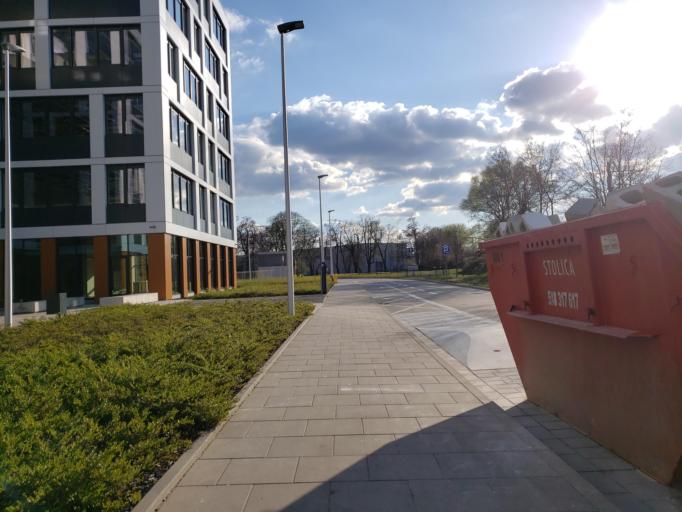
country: PL
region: Lower Silesian Voivodeship
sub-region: Powiat wroclawski
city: Wroclaw
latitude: 51.1178
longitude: 16.9943
